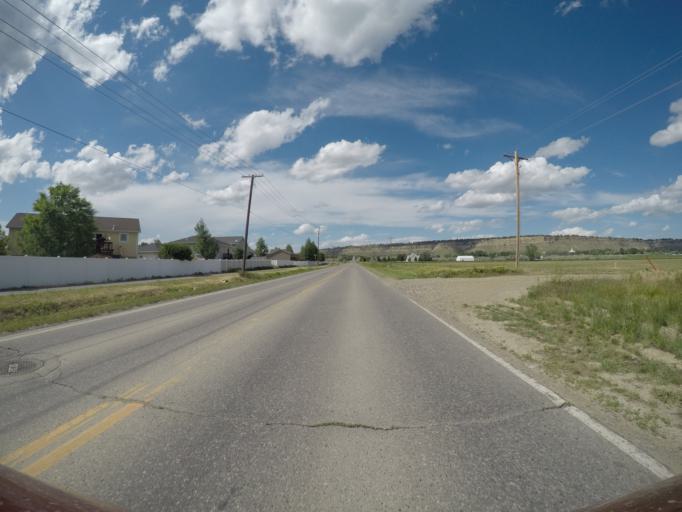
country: US
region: Montana
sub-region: Yellowstone County
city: Billings
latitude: 45.7895
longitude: -108.6527
